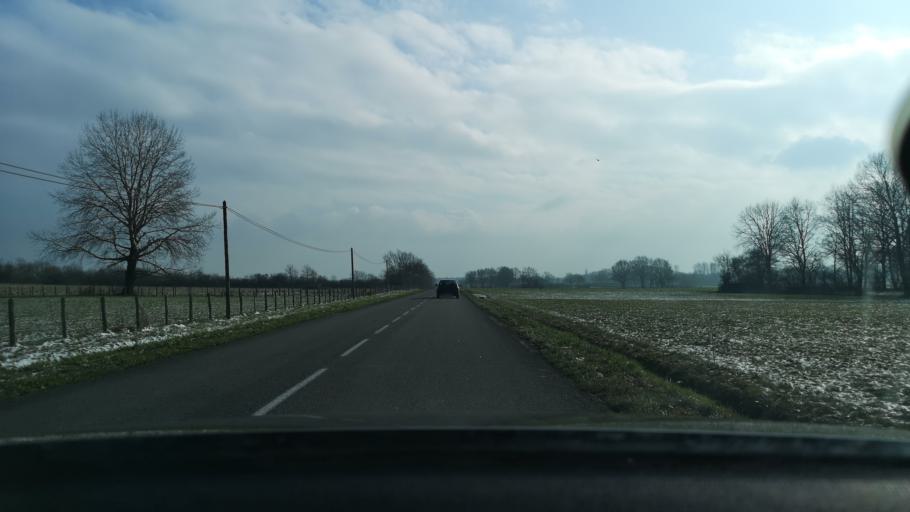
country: FR
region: Bourgogne
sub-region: Departement de Saone-et-Loire
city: Saint-Usuge
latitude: 46.7138
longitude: 5.3174
